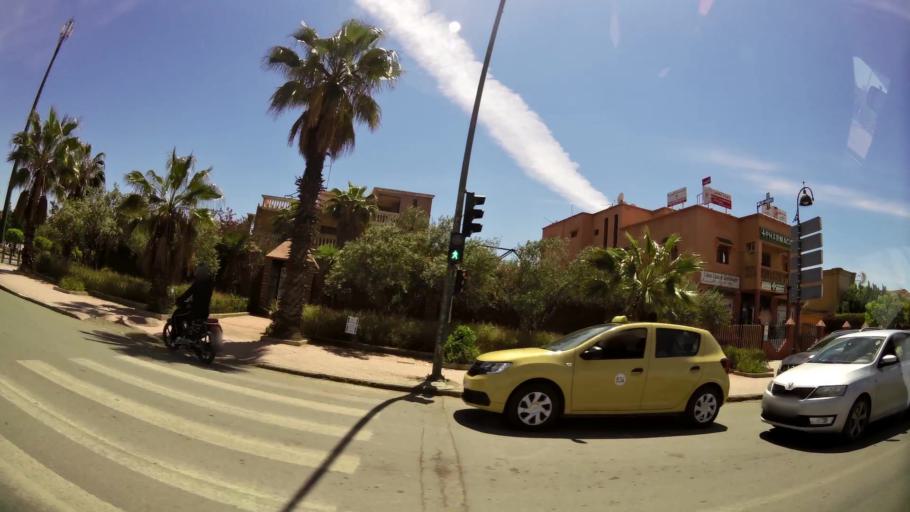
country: MA
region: Marrakech-Tensift-Al Haouz
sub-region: Marrakech
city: Marrakesh
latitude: 31.6386
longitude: -8.0587
